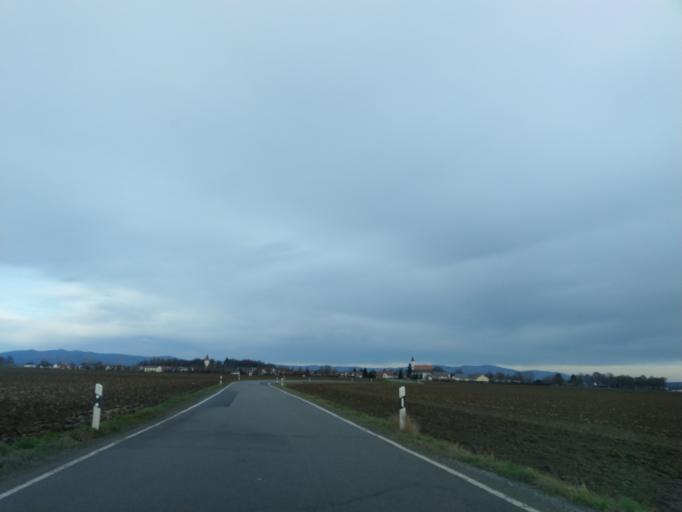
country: DE
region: Bavaria
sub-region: Lower Bavaria
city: Osterhofen
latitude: 48.6830
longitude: 13.0048
